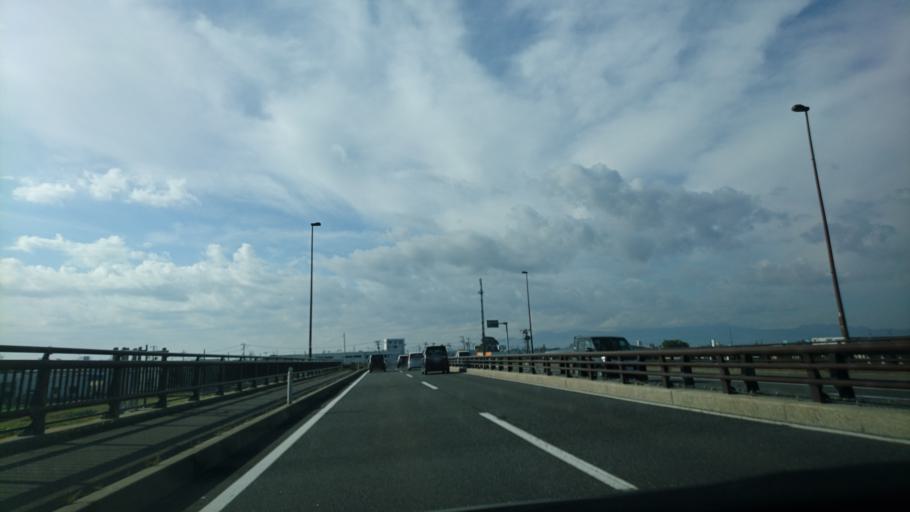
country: JP
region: Miyagi
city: Furukawa
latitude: 38.5946
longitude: 140.9658
